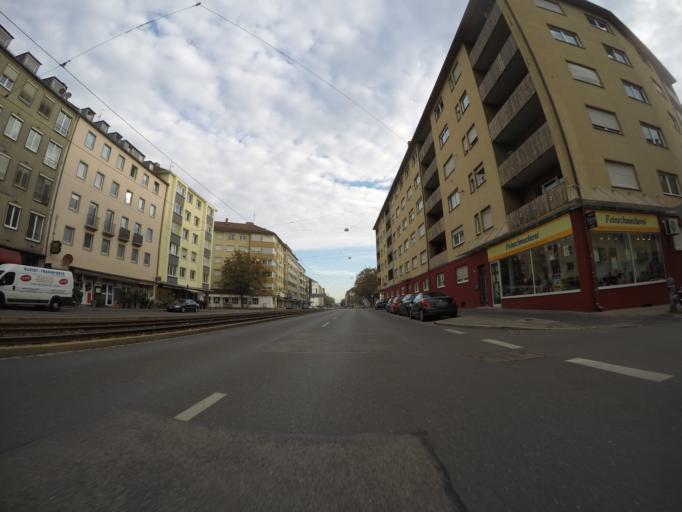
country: DE
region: Bavaria
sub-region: Regierungsbezirk Mittelfranken
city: Nuernberg
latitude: 49.4595
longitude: 11.0906
